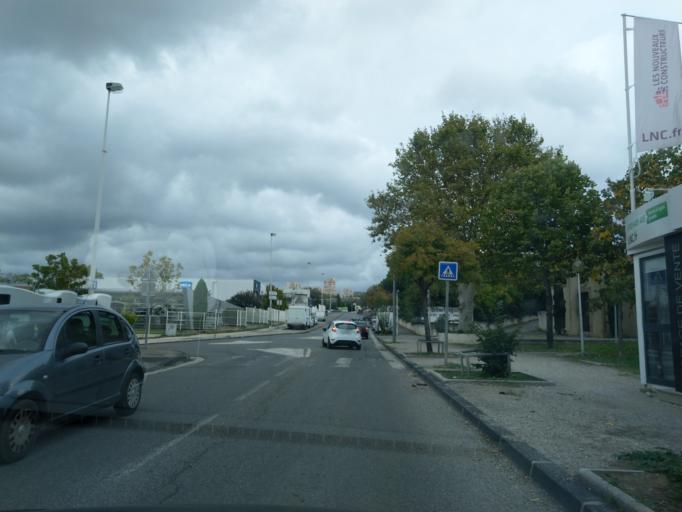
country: FR
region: Provence-Alpes-Cote d'Azur
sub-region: Departement des Bouches-du-Rhone
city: Marseille 12
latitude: 43.2958
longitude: 5.4274
